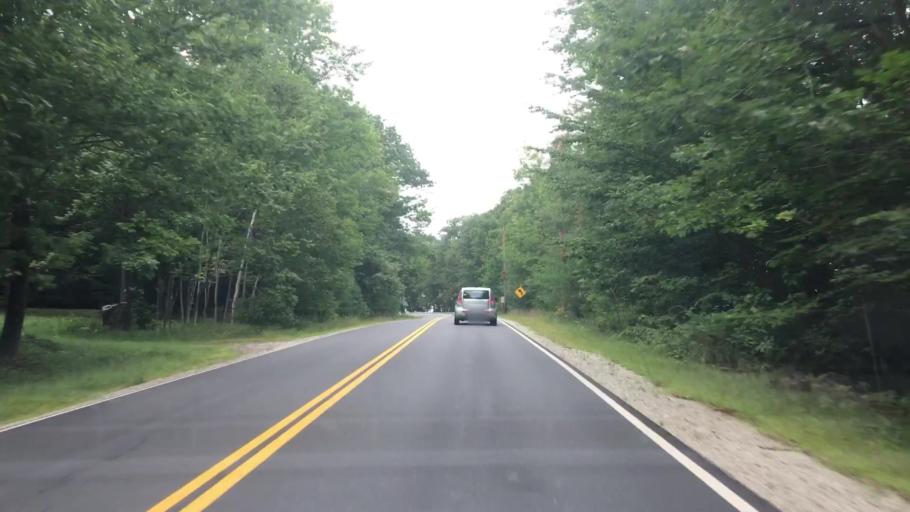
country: US
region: Maine
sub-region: Cumberland County
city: New Gloucester
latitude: 43.8901
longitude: -70.2530
